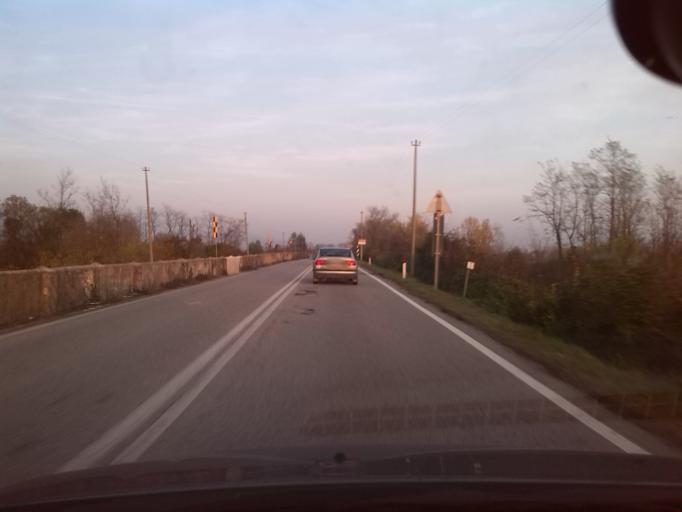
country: IT
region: Friuli Venezia Giulia
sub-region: Provincia di Udine
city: Remanzacco
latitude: 46.0862
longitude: 13.3369
